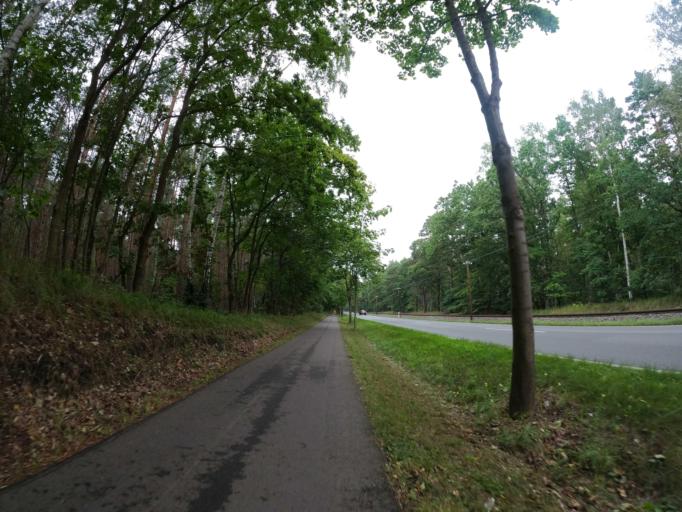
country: DE
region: Mecklenburg-Vorpommern
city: Ostseebad Sellin
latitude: 54.3483
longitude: 13.7061
